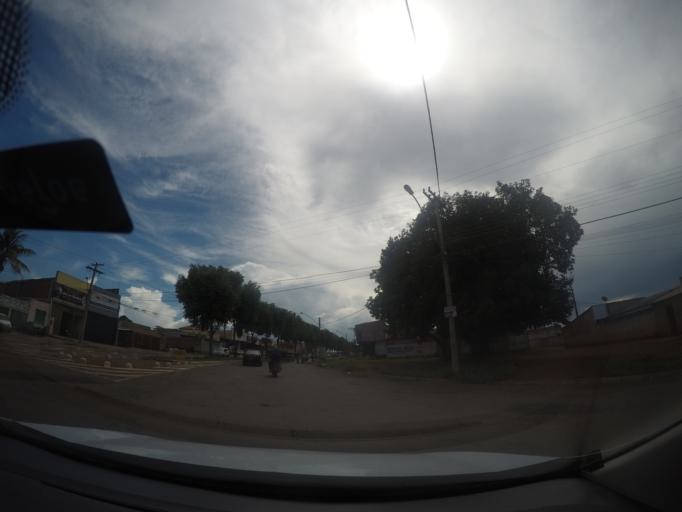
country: BR
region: Goias
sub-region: Trindade
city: Trindade
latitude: -16.6842
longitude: -49.3821
